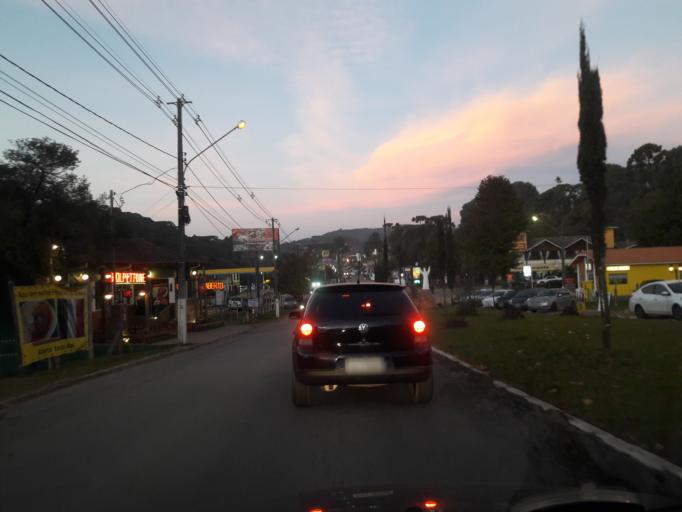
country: BR
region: Minas Gerais
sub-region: Camanducaia
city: Camanducaia
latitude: -22.8647
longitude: -46.0445
